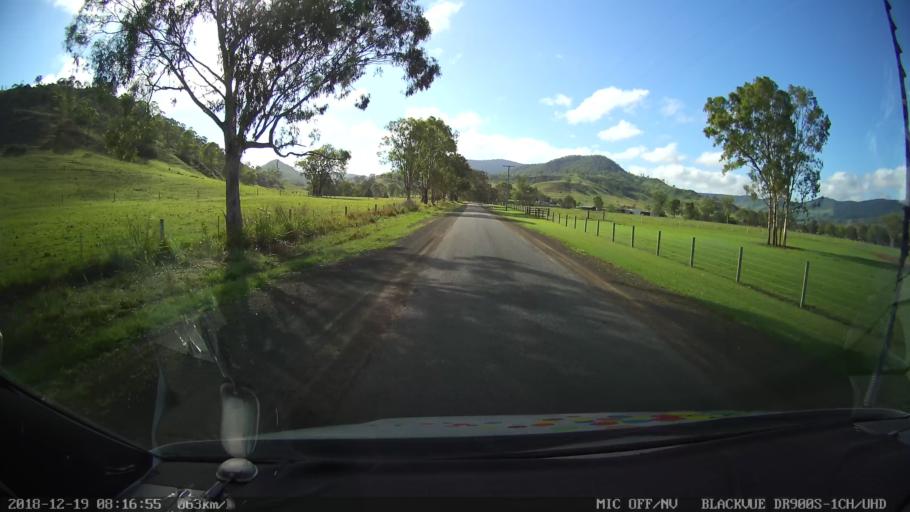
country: AU
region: New South Wales
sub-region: Kyogle
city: Kyogle
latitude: -28.2617
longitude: 152.9082
